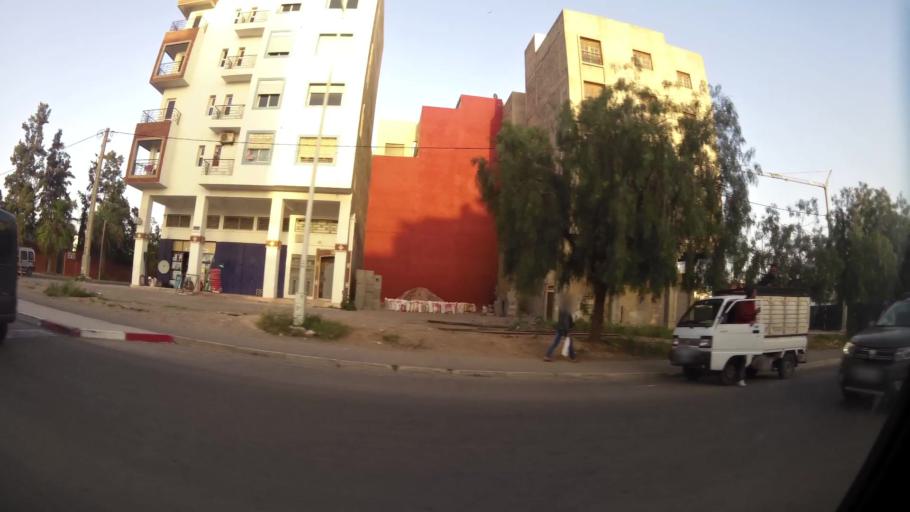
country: MA
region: Oued ed Dahab-Lagouira
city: Dakhla
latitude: 30.3947
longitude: -9.5654
